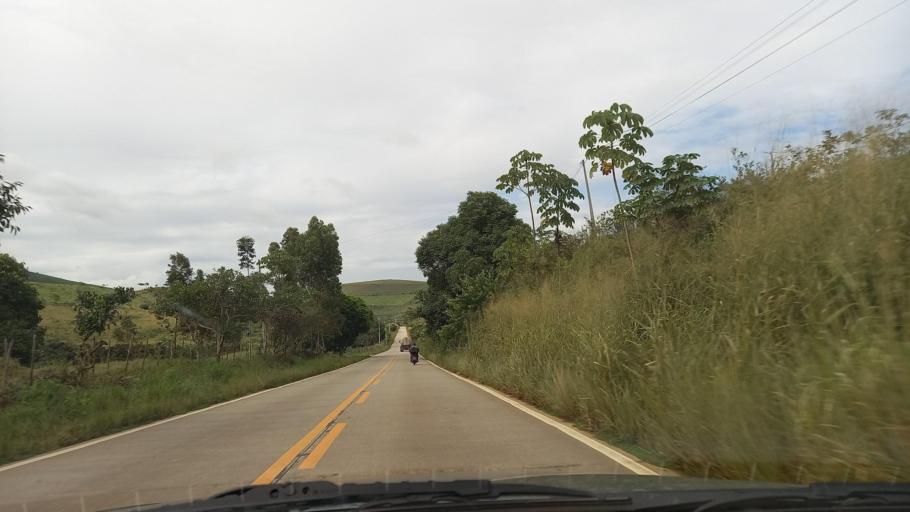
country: BR
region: Pernambuco
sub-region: Maraial
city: Maraial
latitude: -8.7547
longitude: -35.8414
